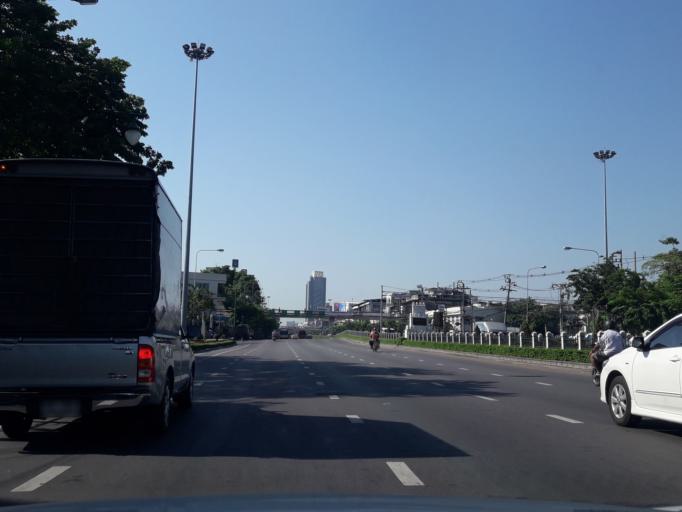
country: TH
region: Bangkok
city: Khlong San
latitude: 13.7350
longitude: 100.4962
